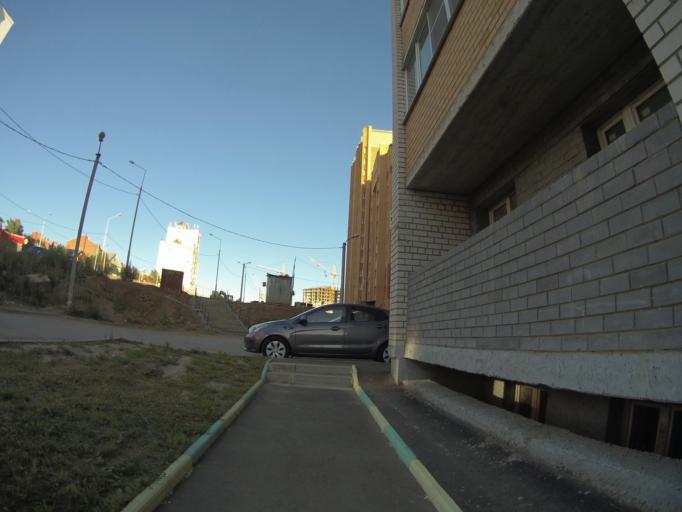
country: RU
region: Vladimir
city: Vladimir
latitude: 56.1067
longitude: 40.3599
